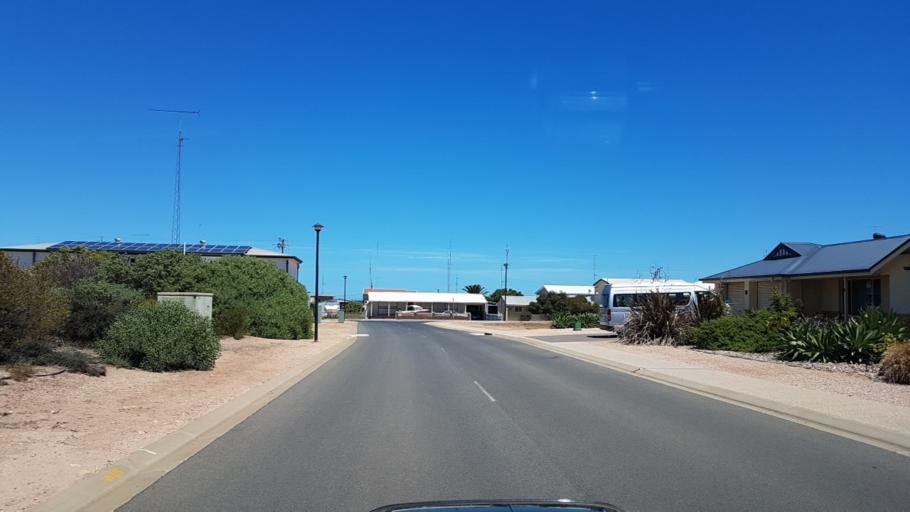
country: AU
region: South Australia
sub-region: Copper Coast
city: Wallaroo
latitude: -33.8949
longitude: 137.6303
